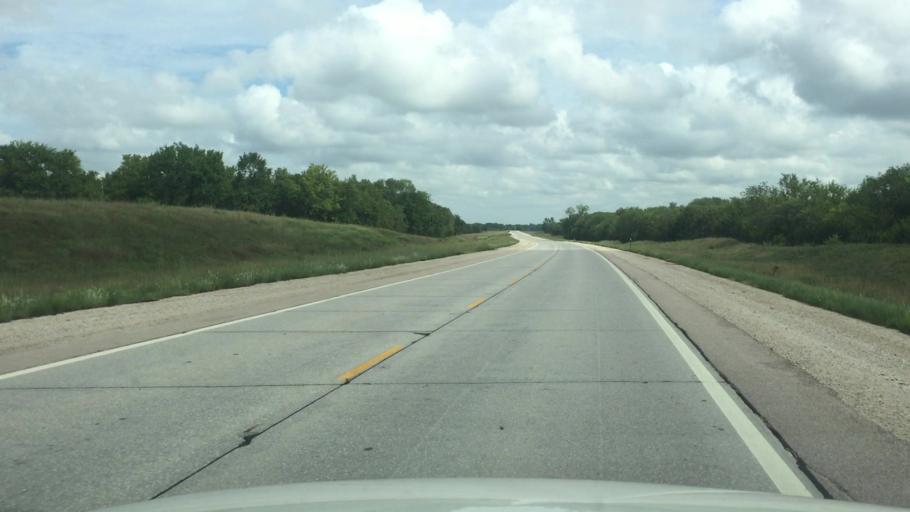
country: US
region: Kansas
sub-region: Allen County
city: Iola
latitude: 37.8989
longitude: -95.3830
